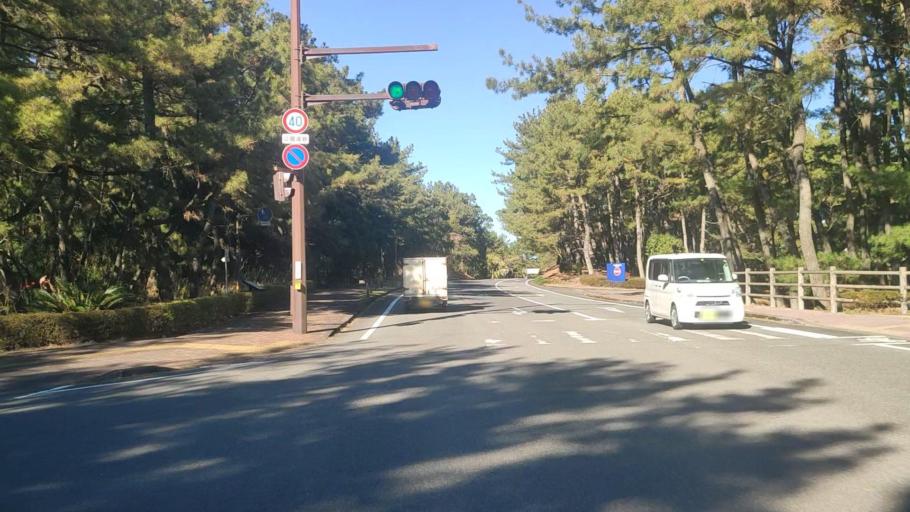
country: JP
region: Miyazaki
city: Miyazaki-shi
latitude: 31.9554
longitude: 131.4672
